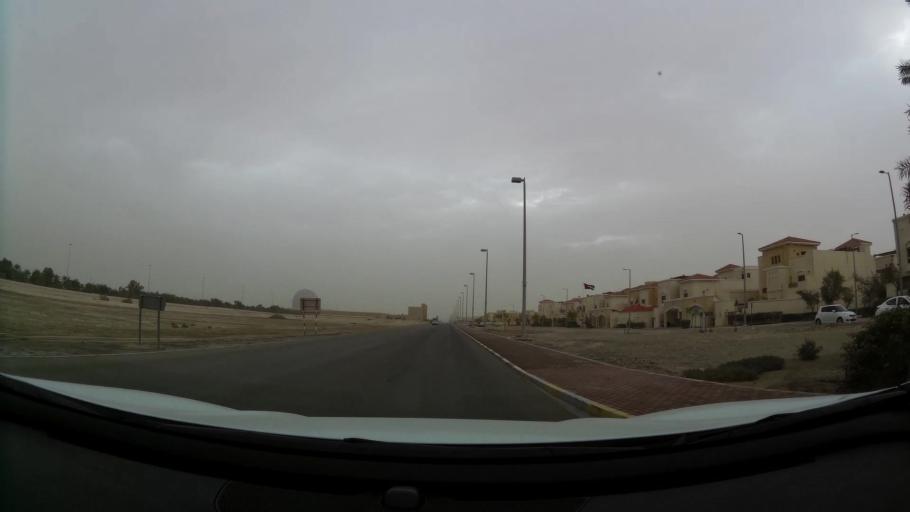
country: AE
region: Abu Dhabi
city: Abu Dhabi
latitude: 24.4314
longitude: 54.5599
